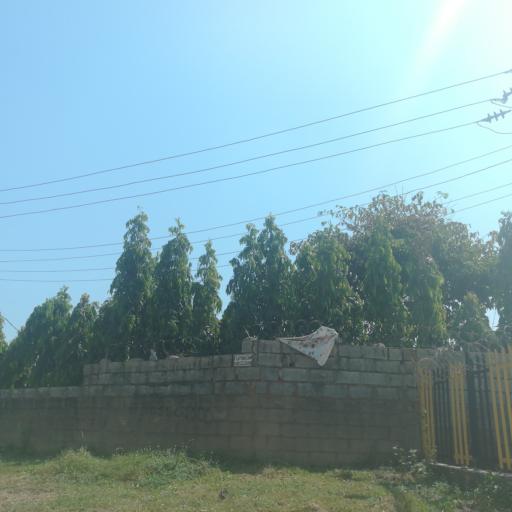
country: NG
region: Abuja Federal Capital Territory
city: Abuja
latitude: 9.0830
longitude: 7.4481
